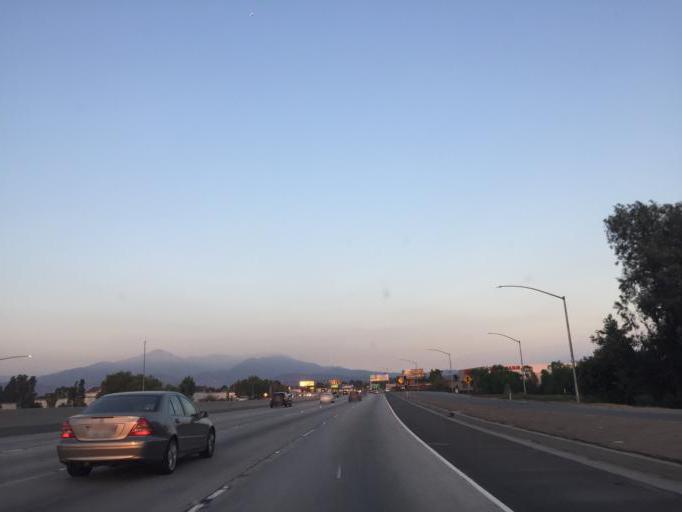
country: US
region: California
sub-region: San Bernardino County
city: Loma Linda
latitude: 34.0641
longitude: -117.2774
